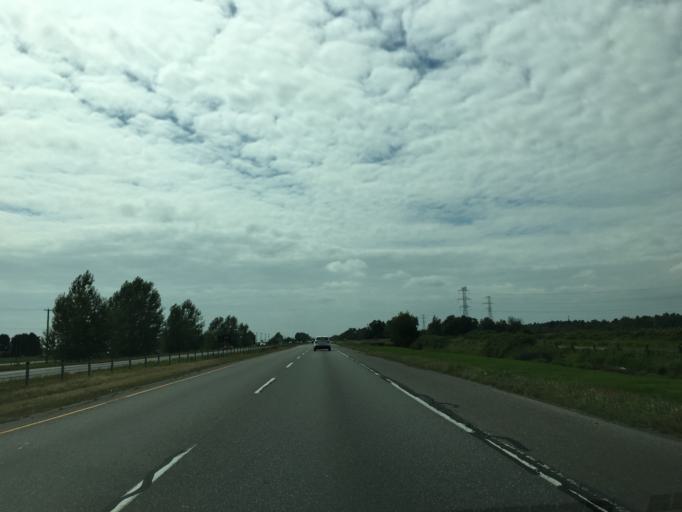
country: CA
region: British Columbia
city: Delta
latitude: 49.0906
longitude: -122.9738
